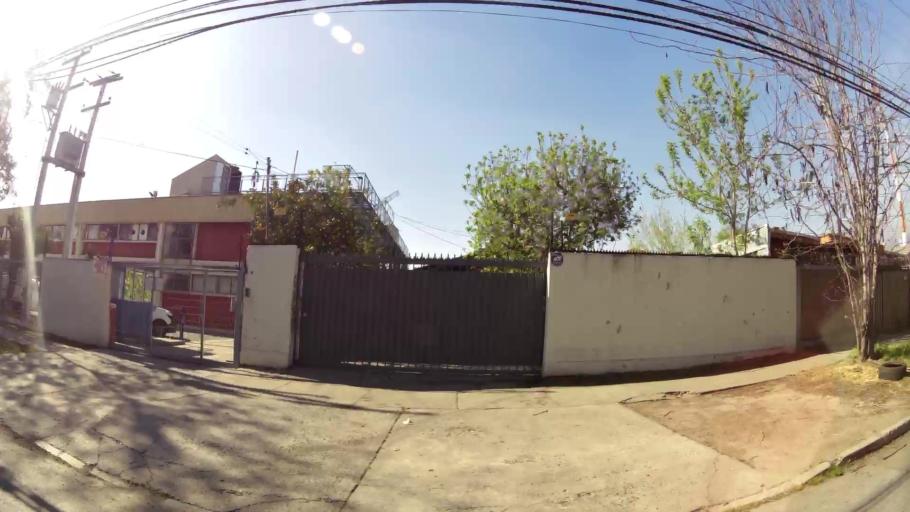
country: CL
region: Santiago Metropolitan
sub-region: Provincia de Santiago
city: Villa Presidente Frei, Nunoa, Santiago, Chile
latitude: -33.4622
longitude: -70.5663
